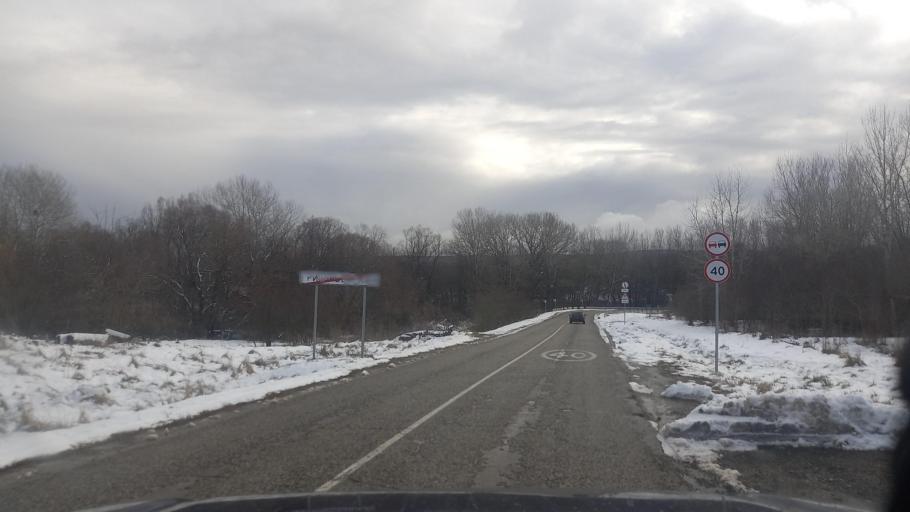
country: RU
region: Krasnodarskiy
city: Smolenskaya
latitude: 44.7730
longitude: 38.8460
